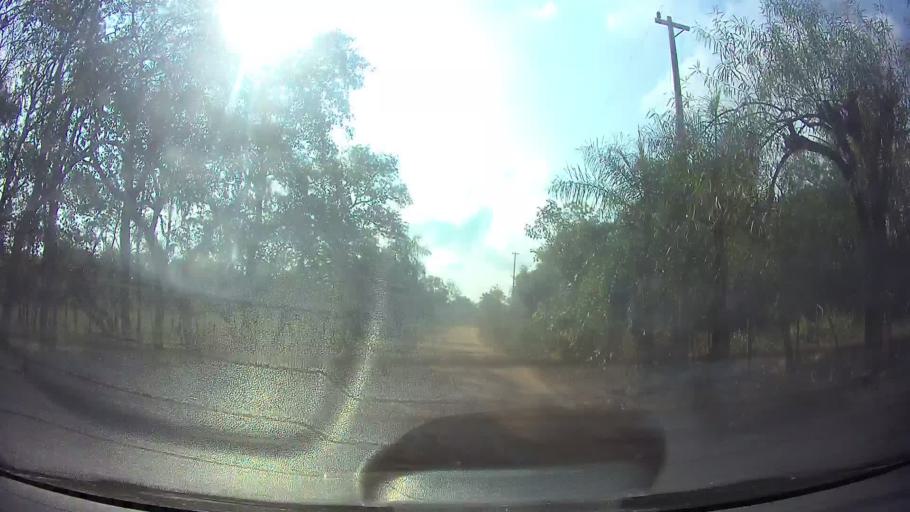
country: PY
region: Cordillera
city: Arroyos y Esteros
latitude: -25.0462
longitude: -57.1878
